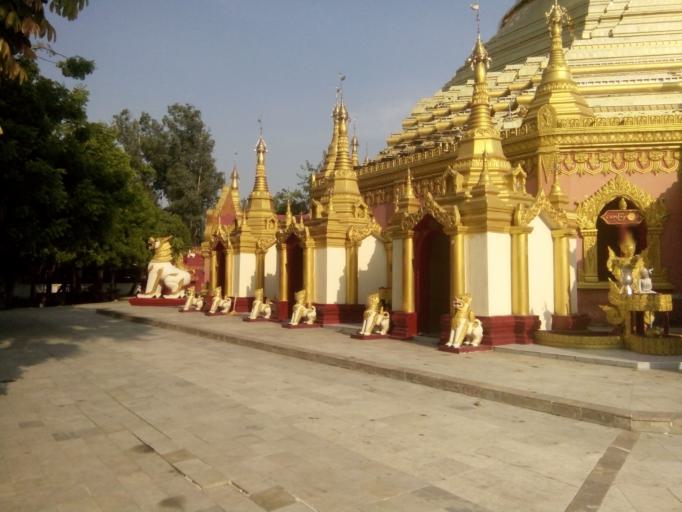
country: MM
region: Yangon
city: Yangon
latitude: 16.9318
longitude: 96.1552
